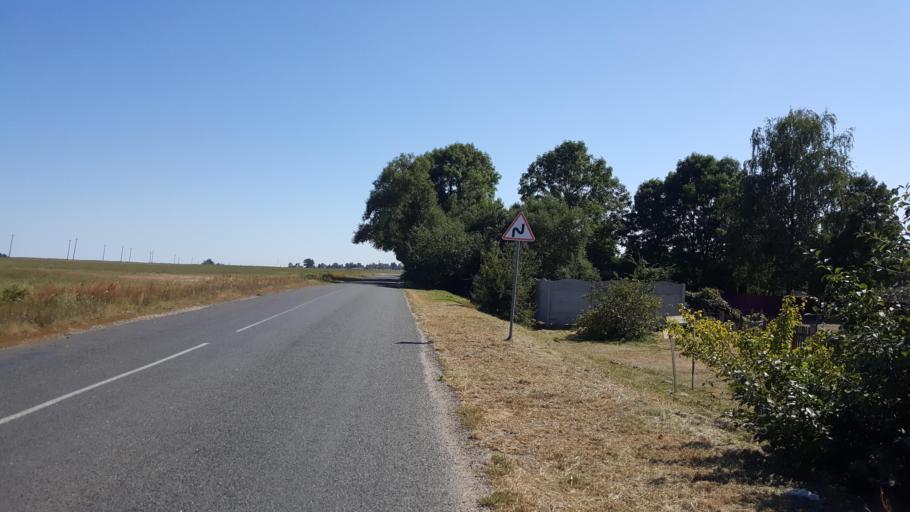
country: PL
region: Lublin Voivodeship
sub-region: Powiat bialski
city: Terespol
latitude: 52.2119
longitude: 23.5207
